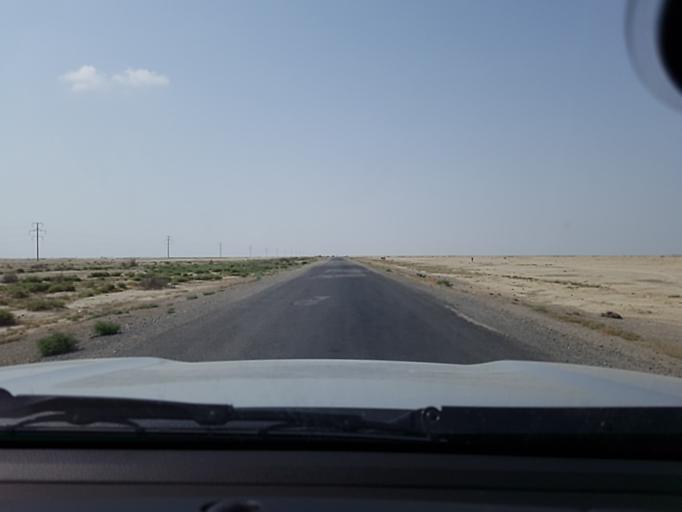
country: TM
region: Balkan
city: Gumdag
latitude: 38.8961
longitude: 54.5926
